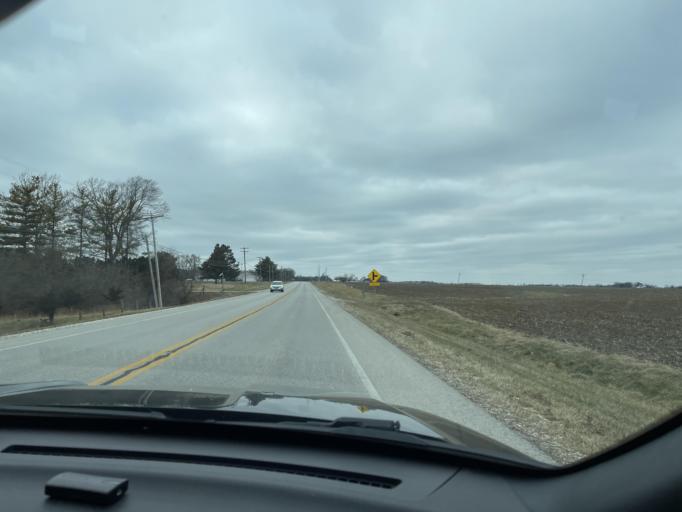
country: US
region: Illinois
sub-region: Sangamon County
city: Leland Grove
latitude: 39.8194
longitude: -89.7167
